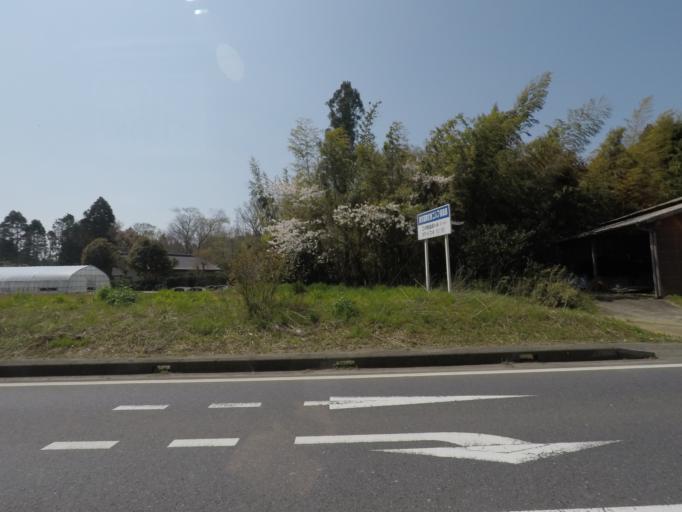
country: JP
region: Chiba
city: Naruto
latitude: 35.6692
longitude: 140.4368
